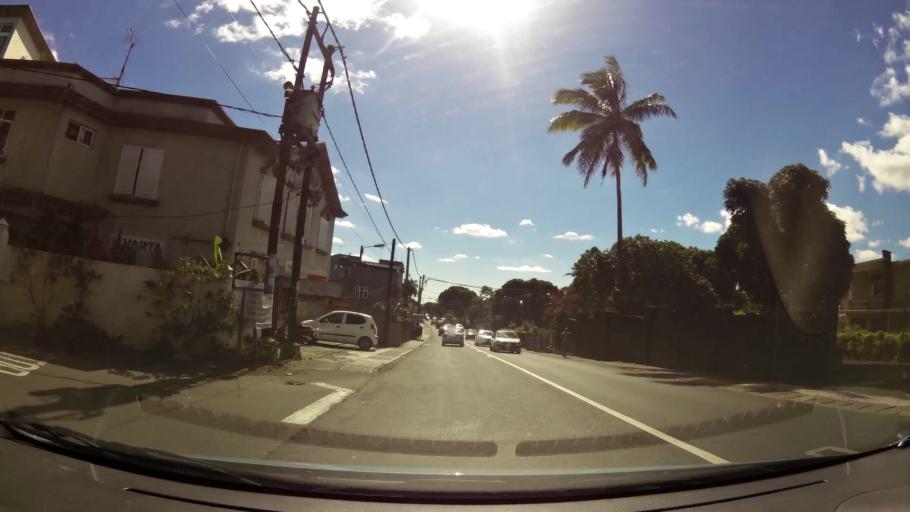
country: MU
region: Plaines Wilhems
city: Vacoas
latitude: -20.2873
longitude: 57.4810
